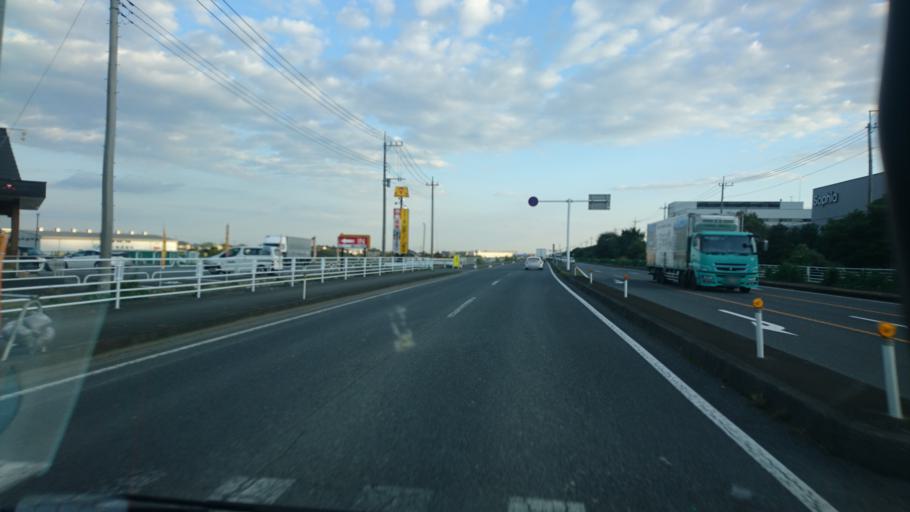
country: JP
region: Gunma
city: Ota
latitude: 36.3576
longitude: 139.3735
